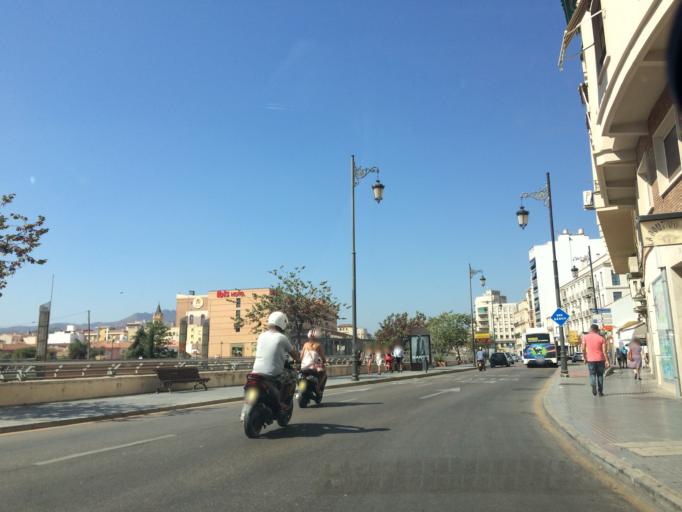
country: ES
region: Andalusia
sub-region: Provincia de Malaga
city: Malaga
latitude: 36.7192
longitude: -4.4252
